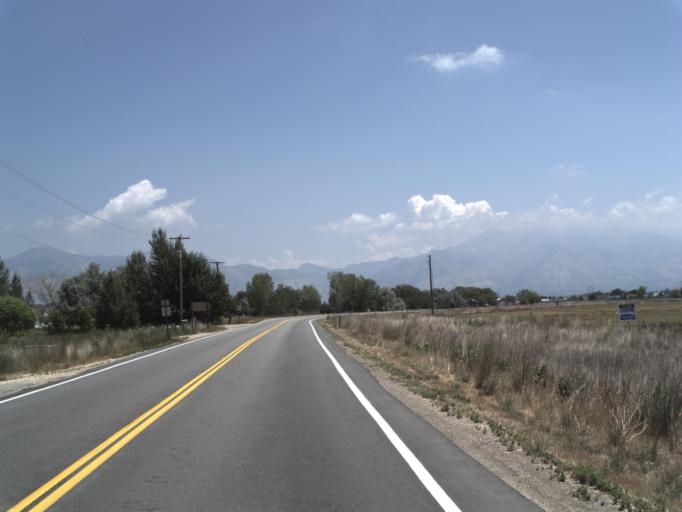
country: US
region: Utah
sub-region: Weber County
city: Plain City
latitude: 41.2459
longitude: -112.0927
